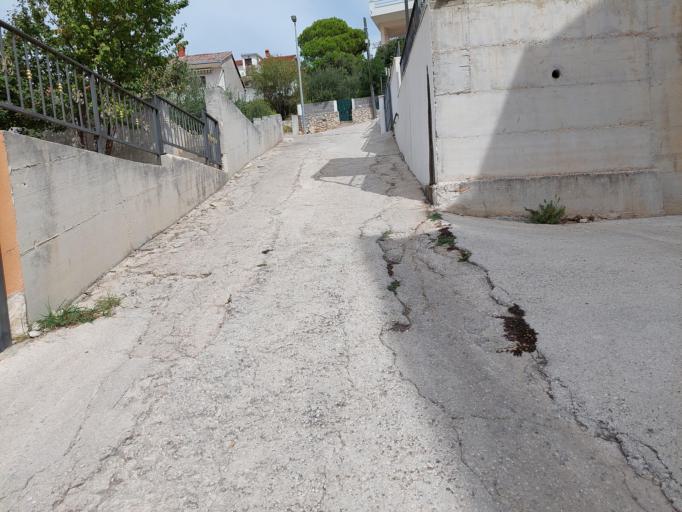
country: HR
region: Splitsko-Dalmatinska
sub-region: Grad Trogir
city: Trogir
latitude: 43.4898
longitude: 16.2798
